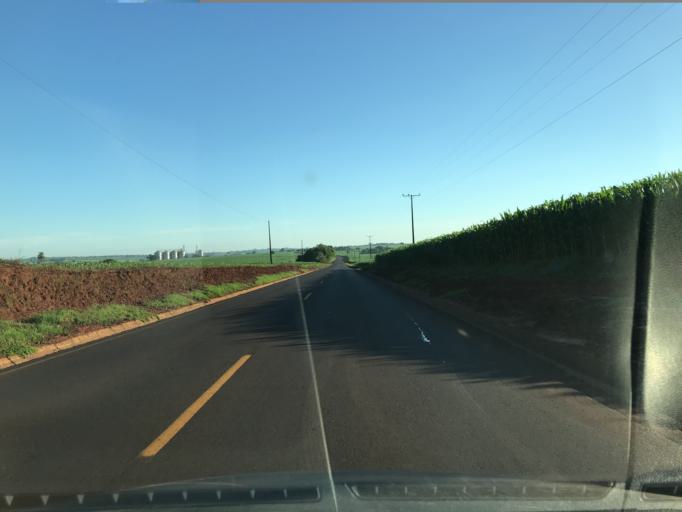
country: BR
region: Parana
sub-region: Palotina
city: Palotina
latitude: -24.1313
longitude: -53.8535
